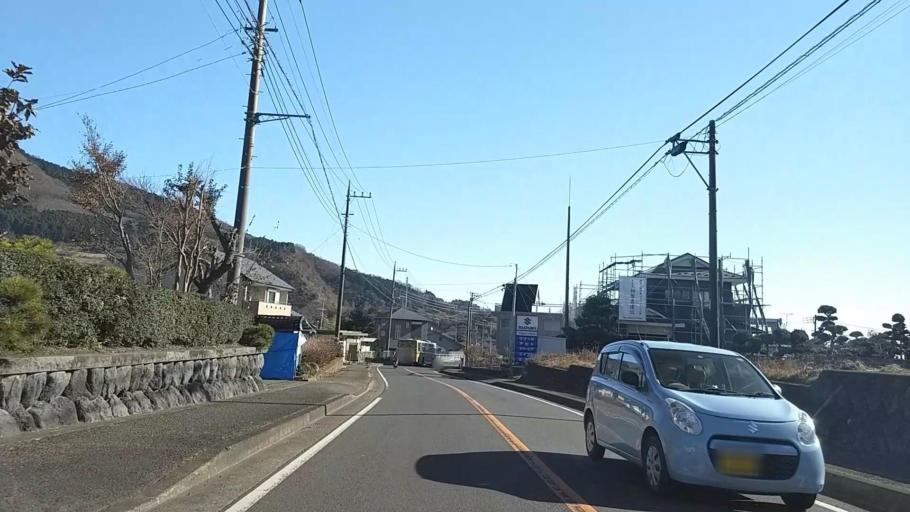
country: JP
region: Kanagawa
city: Hadano
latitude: 35.4004
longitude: 139.1920
